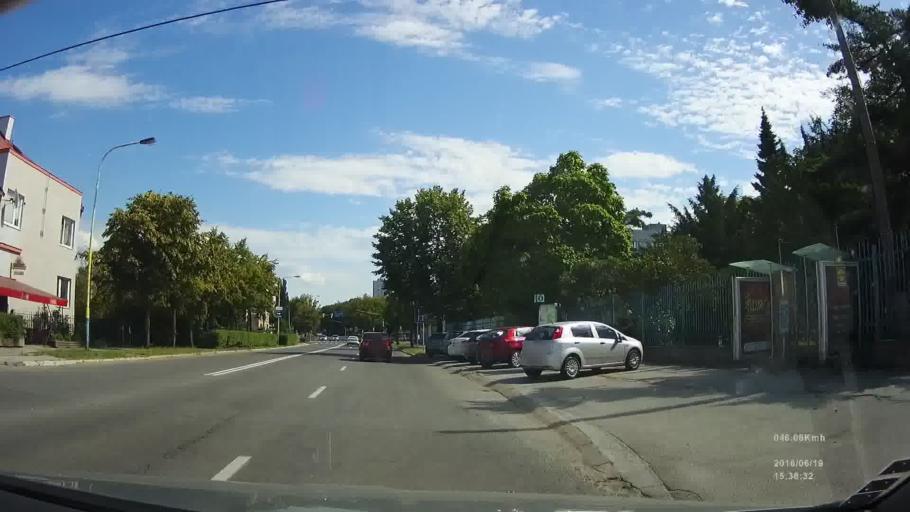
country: SK
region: Kosicky
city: Kosice
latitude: 48.7089
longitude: 21.2572
